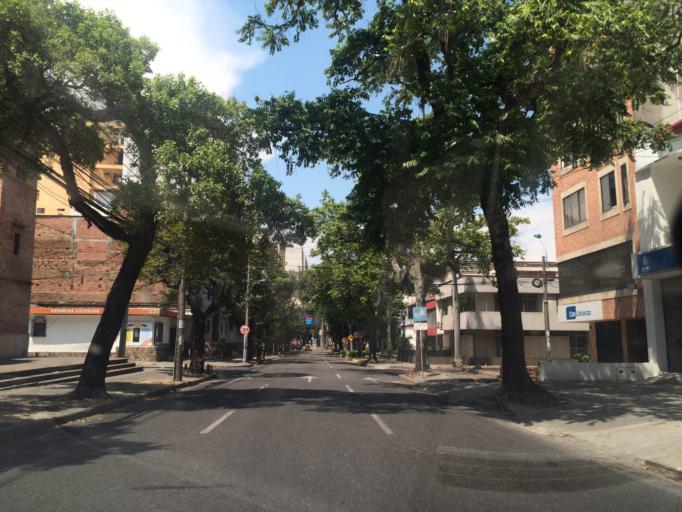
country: CO
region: Valle del Cauca
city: Cali
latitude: 3.4528
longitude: -76.5375
